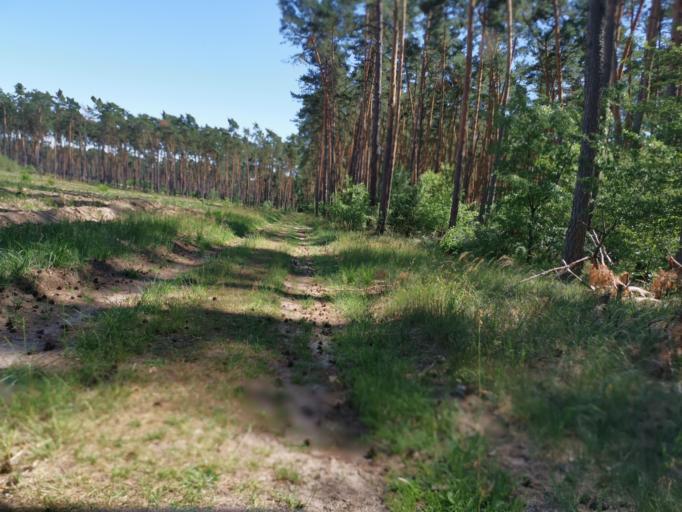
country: CZ
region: South Moravian
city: Rohatec
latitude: 48.9079
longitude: 17.2181
